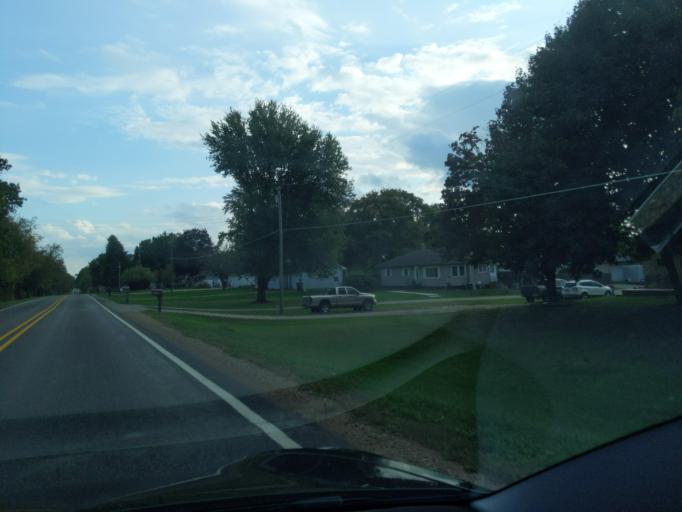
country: US
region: Michigan
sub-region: Jackson County
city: Jackson
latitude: 42.3103
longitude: -84.4628
